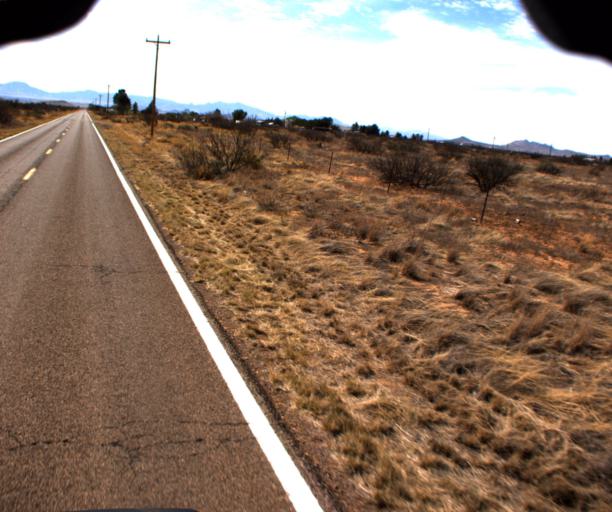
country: US
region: Arizona
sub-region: Cochise County
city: Willcox
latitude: 31.8762
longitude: -109.6176
